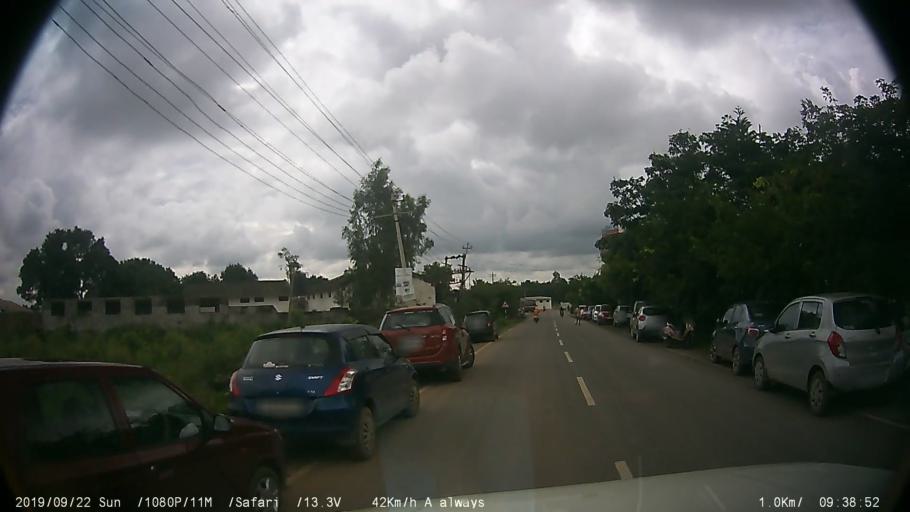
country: IN
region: Karnataka
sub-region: Bangalore Urban
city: Anekal
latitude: 12.8187
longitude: 77.6268
